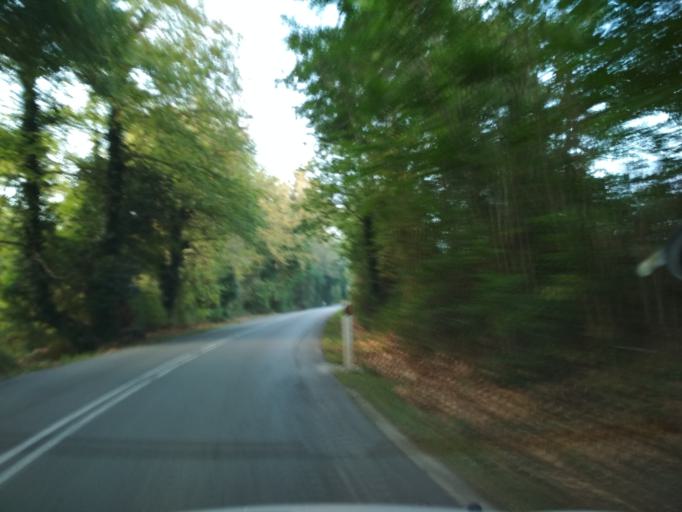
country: GR
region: Central Greece
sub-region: Nomos Evvoias
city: Prokopion
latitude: 38.7470
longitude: 23.4889
